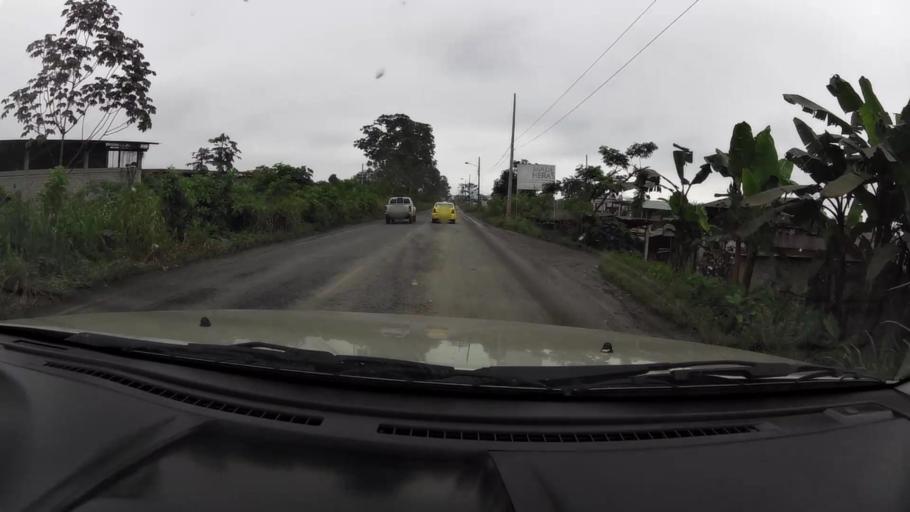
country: EC
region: Guayas
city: Balao
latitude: -3.0702
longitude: -79.7509
